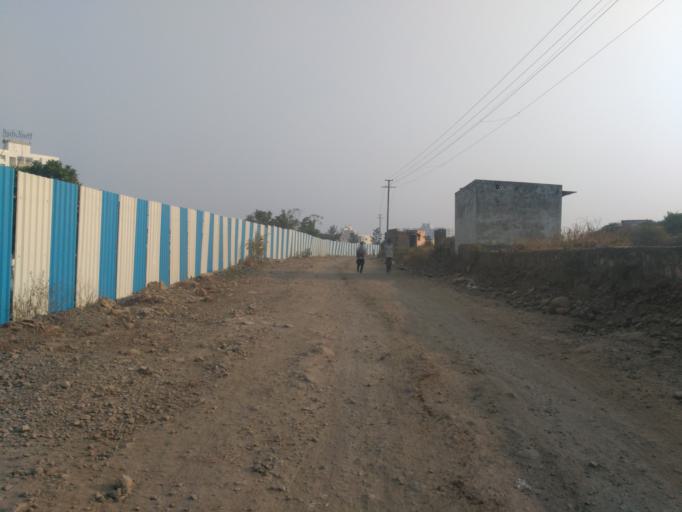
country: IN
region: Maharashtra
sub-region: Pune Division
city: Pune
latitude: 18.4322
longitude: 73.8875
